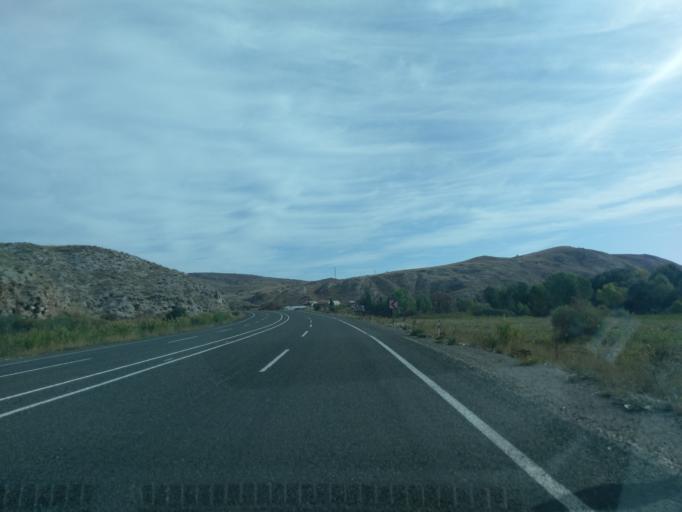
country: TR
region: Sivas
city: Zara
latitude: 39.8553
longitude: 37.8671
